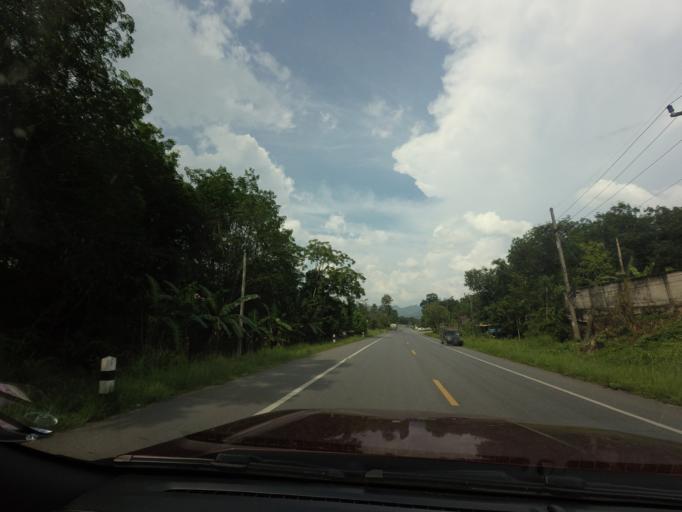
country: TH
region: Yala
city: Ban Nang Sata
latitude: 6.2569
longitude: 101.2397
